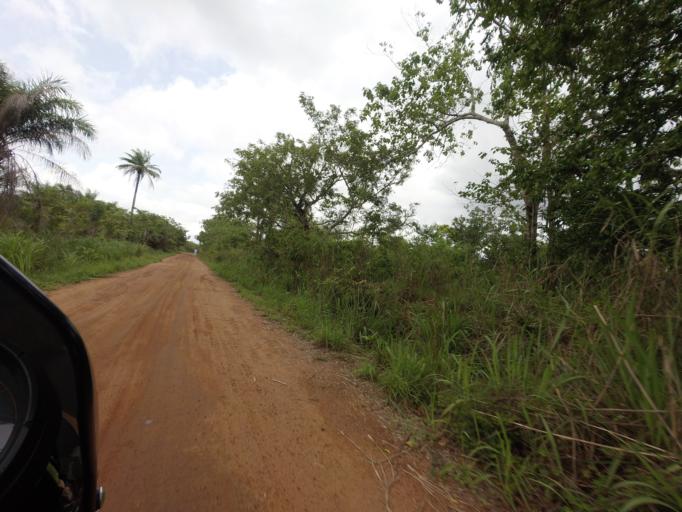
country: SL
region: Northern Province
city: Kassiri
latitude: 9.0331
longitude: -13.0702
